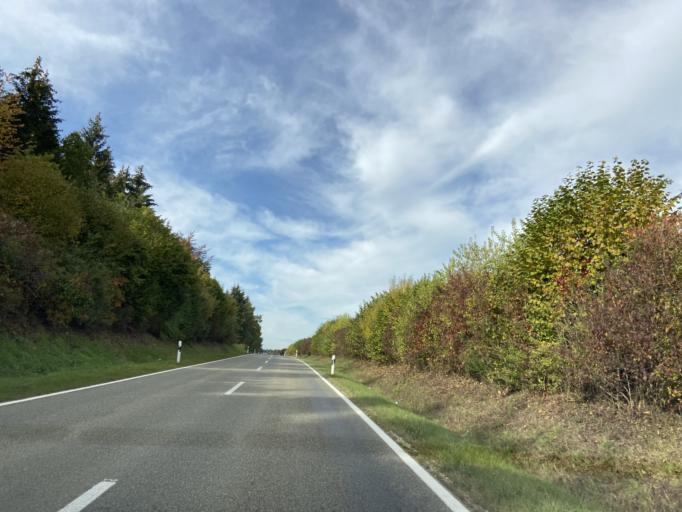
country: DE
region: Baden-Wuerttemberg
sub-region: Tuebingen Region
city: Messkirch
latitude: 48.0498
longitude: 9.0954
